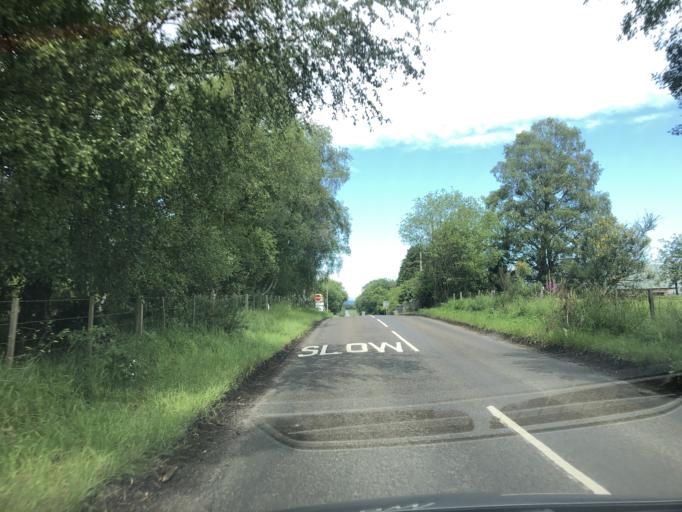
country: GB
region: Scotland
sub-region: Angus
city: Forfar
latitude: 56.6865
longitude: -2.9365
